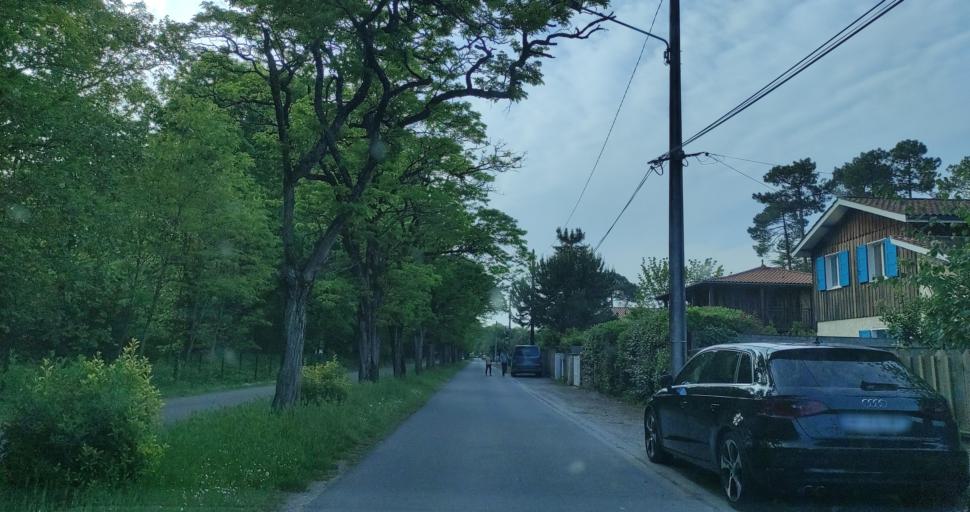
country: FR
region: Aquitaine
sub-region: Departement de la Gironde
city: Ares
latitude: 44.7551
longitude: -1.1302
